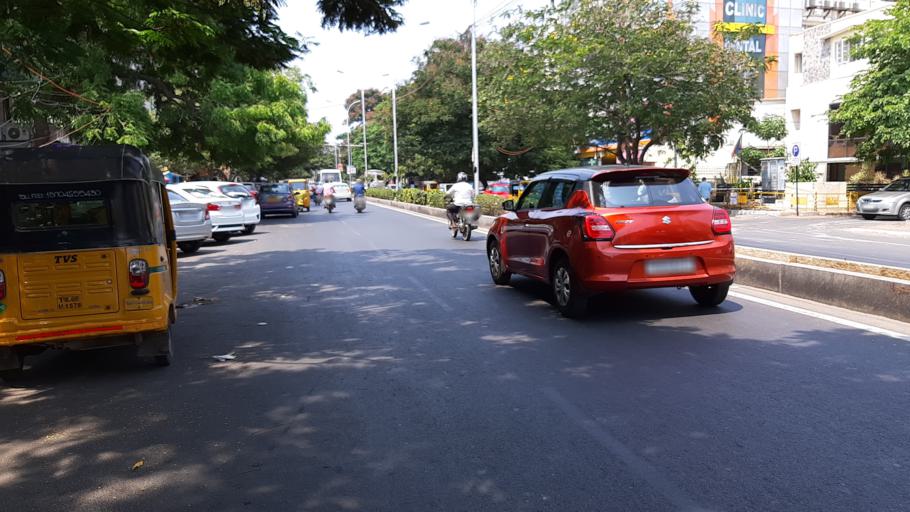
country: IN
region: Tamil Nadu
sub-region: Chennai
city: Chetput
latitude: 13.0466
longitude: 80.2428
